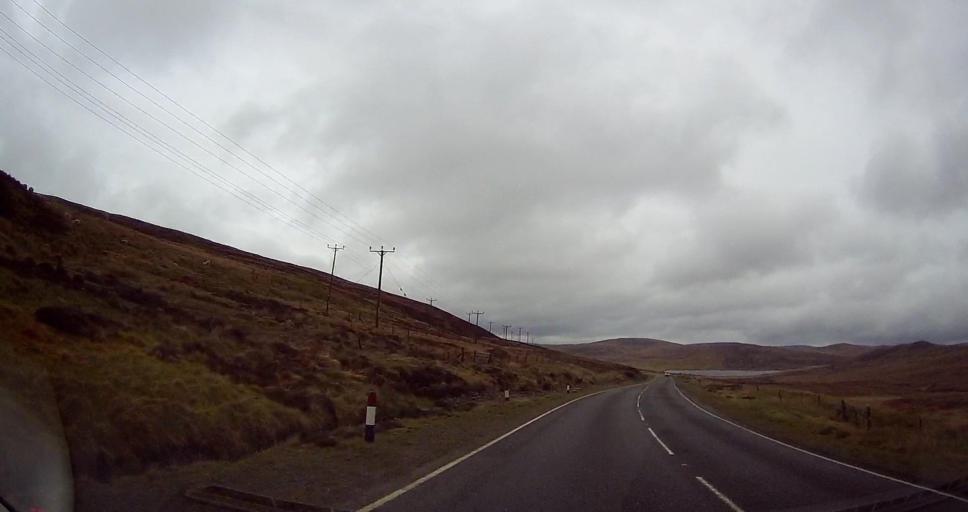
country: GB
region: Scotland
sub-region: Shetland Islands
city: Lerwick
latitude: 60.3330
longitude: -1.2533
